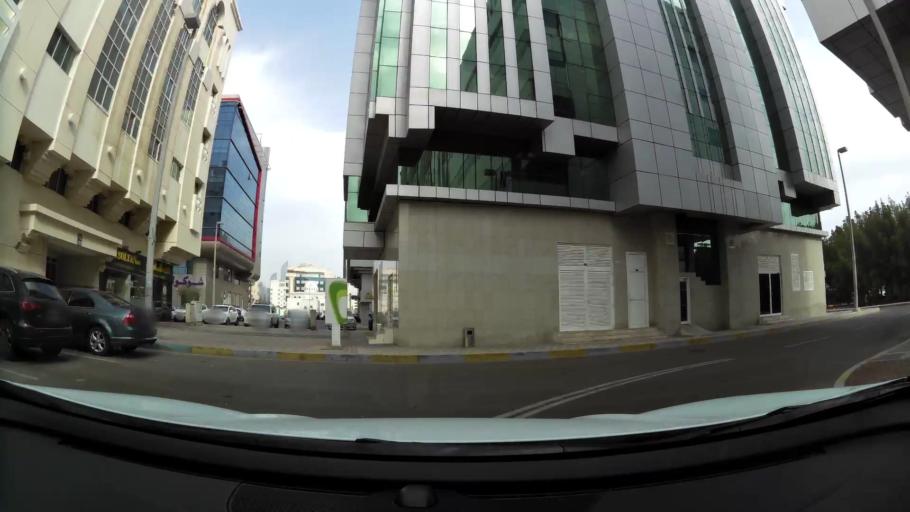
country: AE
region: Abu Dhabi
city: Abu Dhabi
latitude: 24.4692
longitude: 54.3813
